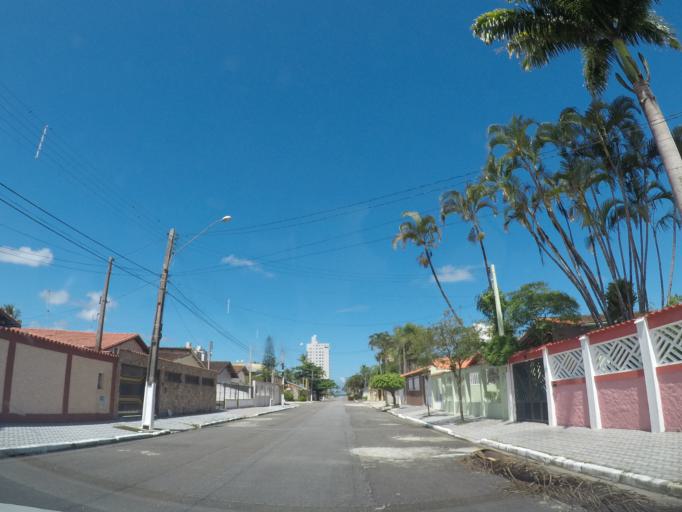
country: BR
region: Sao Paulo
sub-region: Mongagua
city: Mongagua
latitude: -24.0681
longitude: -46.5701
